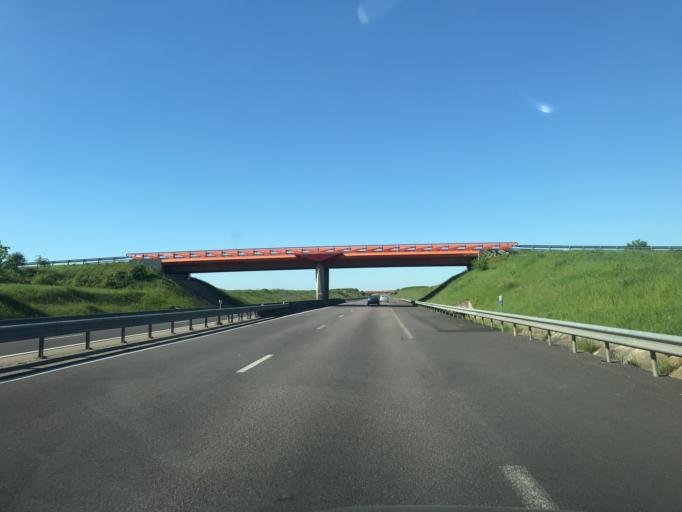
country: FR
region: Haute-Normandie
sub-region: Departement de l'Eure
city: Evreux
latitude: 48.9645
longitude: 1.1984
